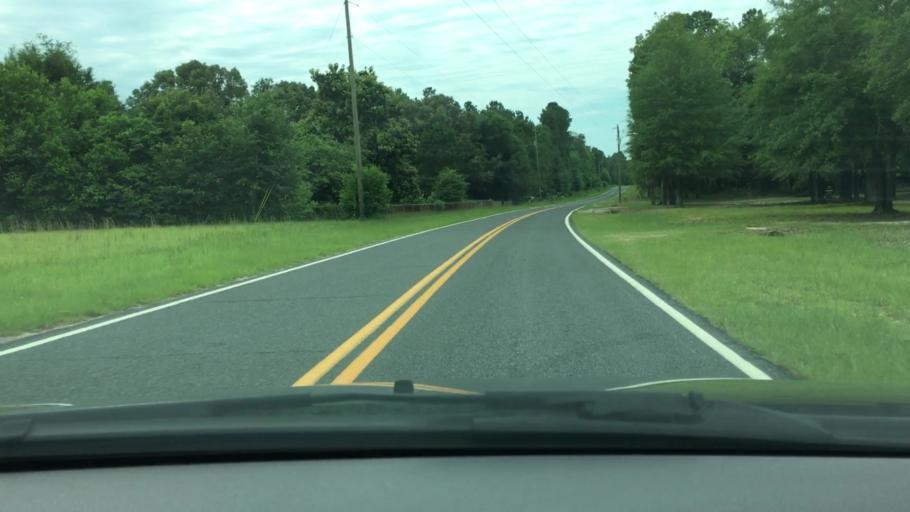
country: US
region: South Carolina
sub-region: Barnwell County
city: Williston
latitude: 33.6366
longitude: -81.3635
